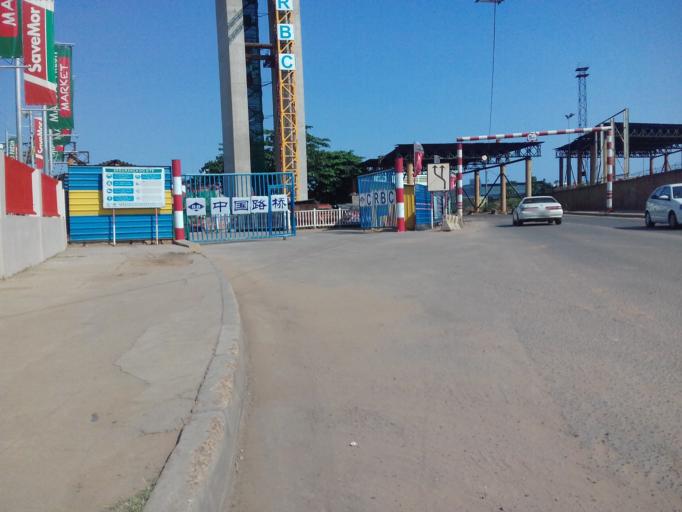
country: MZ
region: Maputo City
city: Maputo
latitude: -25.9656
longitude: 32.5593
